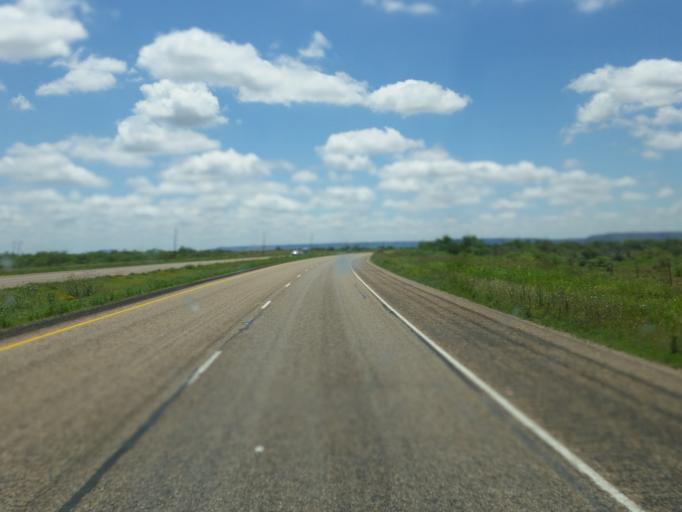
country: US
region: Texas
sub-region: Garza County
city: Post
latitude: 33.0906
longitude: -101.2454
